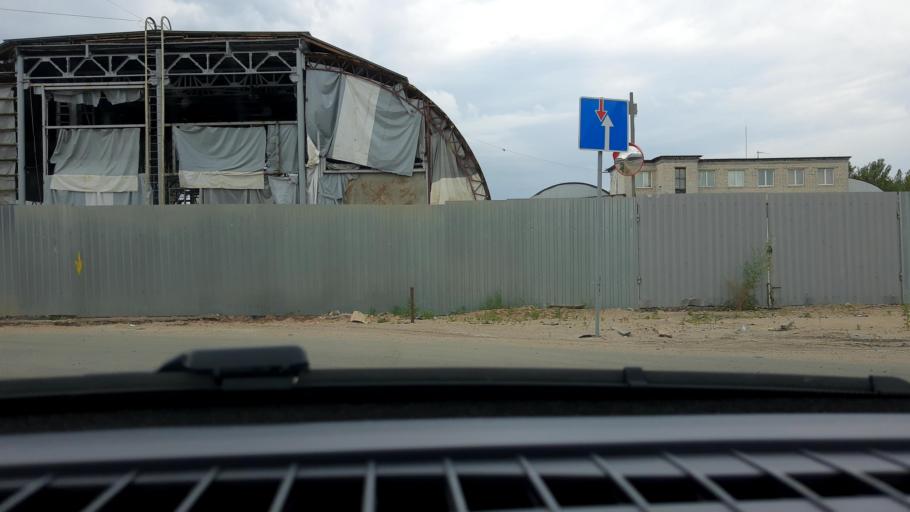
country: RU
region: Nizjnij Novgorod
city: Gorbatovka
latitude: 56.3200
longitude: 43.8484
